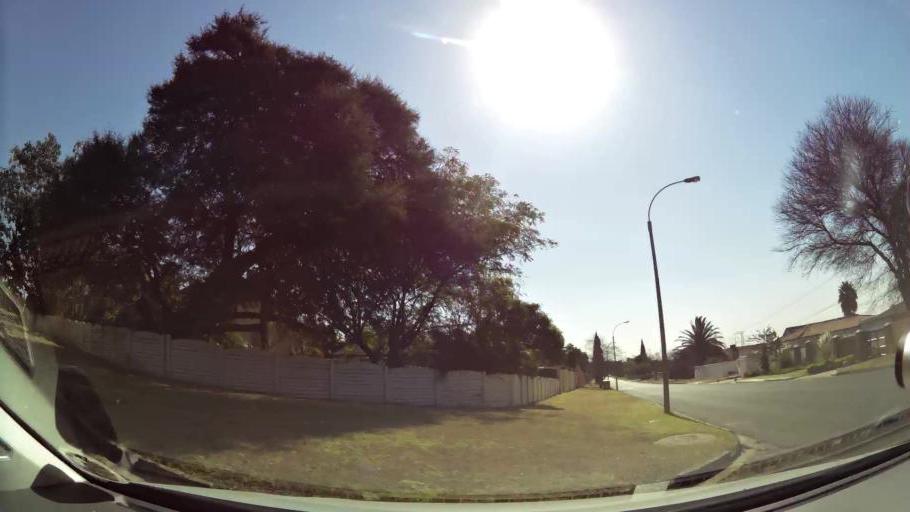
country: ZA
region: Gauteng
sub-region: City of Johannesburg Metropolitan Municipality
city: Modderfontein
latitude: -26.0555
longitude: 28.2126
